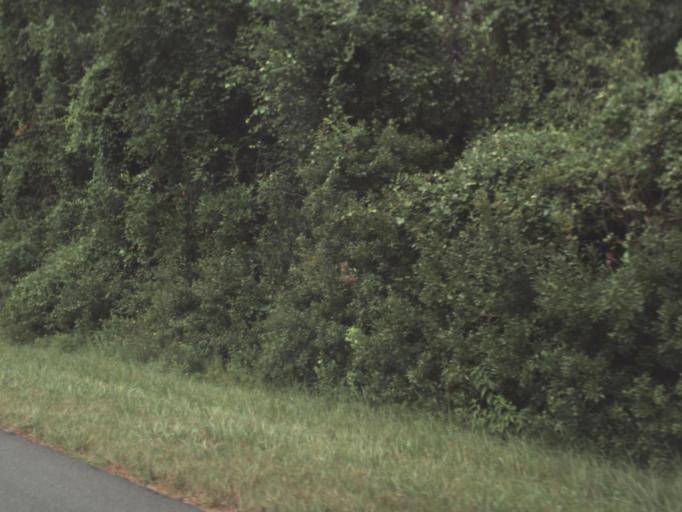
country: US
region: Florida
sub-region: Hamilton County
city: Jasper
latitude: 30.5727
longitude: -82.6798
